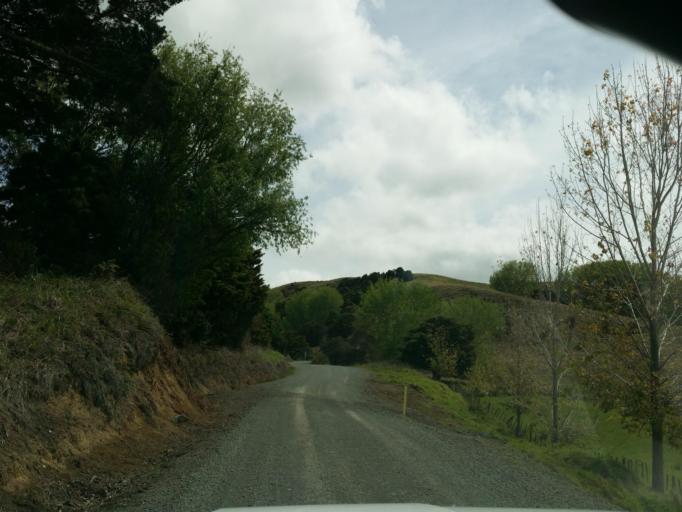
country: NZ
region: Northland
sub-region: Whangarei
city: Maungatapere
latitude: -35.9035
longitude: 174.1245
